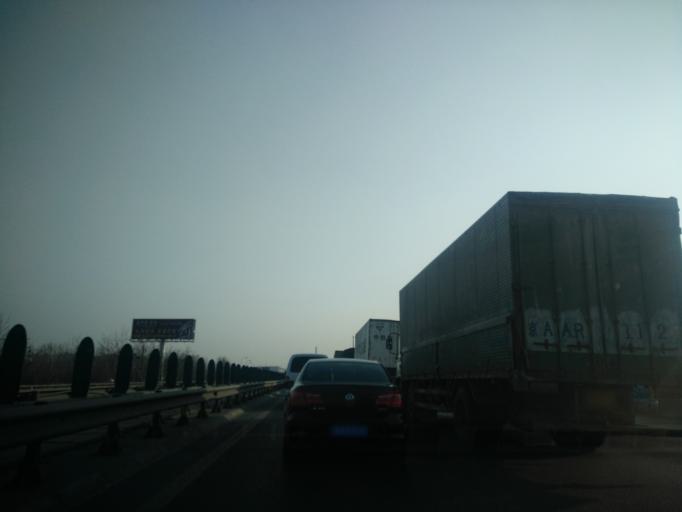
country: CN
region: Beijing
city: Dongfeng
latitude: 39.8673
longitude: 116.5424
